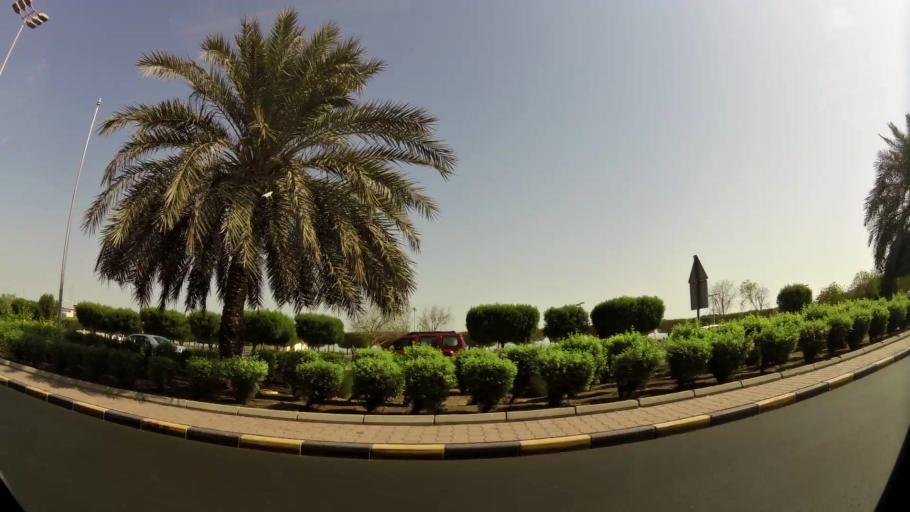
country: KW
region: Al Asimah
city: Ad Dasmah
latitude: 29.3860
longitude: 48.0022
